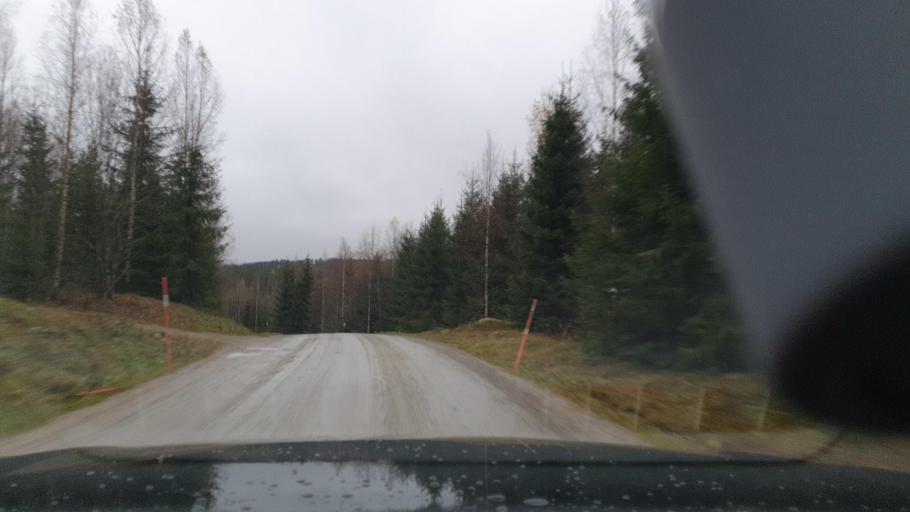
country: SE
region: Vaermland
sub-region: Arvika Kommun
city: Arvika
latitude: 59.8228
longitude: 12.7427
